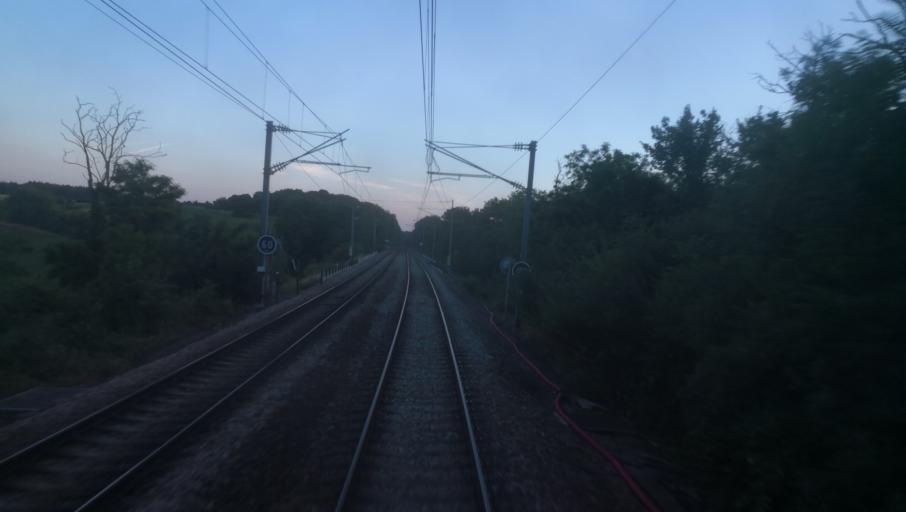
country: FR
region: Ile-de-France
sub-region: Departement des Yvelines
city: Rosny-sur-Seine
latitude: 48.9813
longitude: 1.6195
